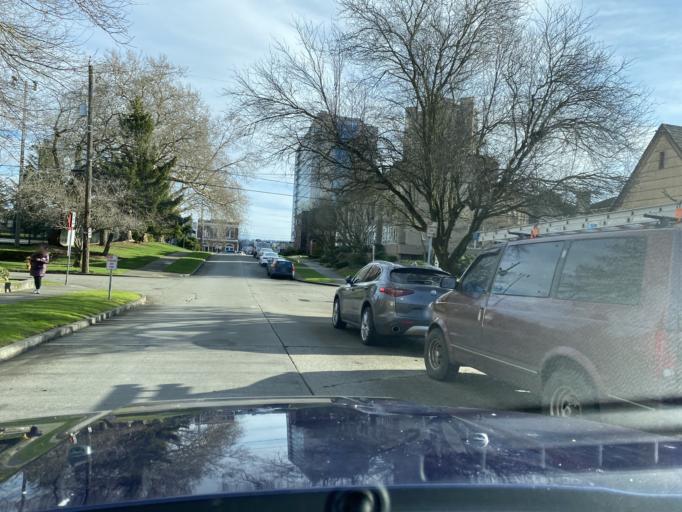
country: US
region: Washington
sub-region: King County
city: Medina
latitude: 47.6346
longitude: -122.2789
